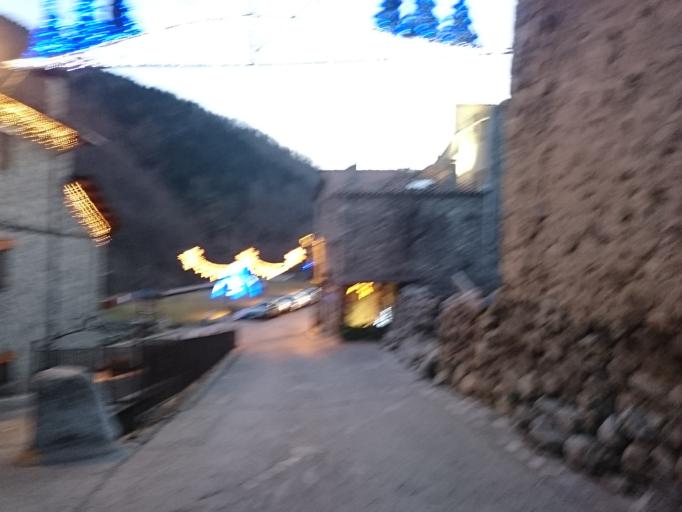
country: ES
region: Catalonia
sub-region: Provincia de Girona
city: Camprodon
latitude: 42.3755
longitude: 2.3019
